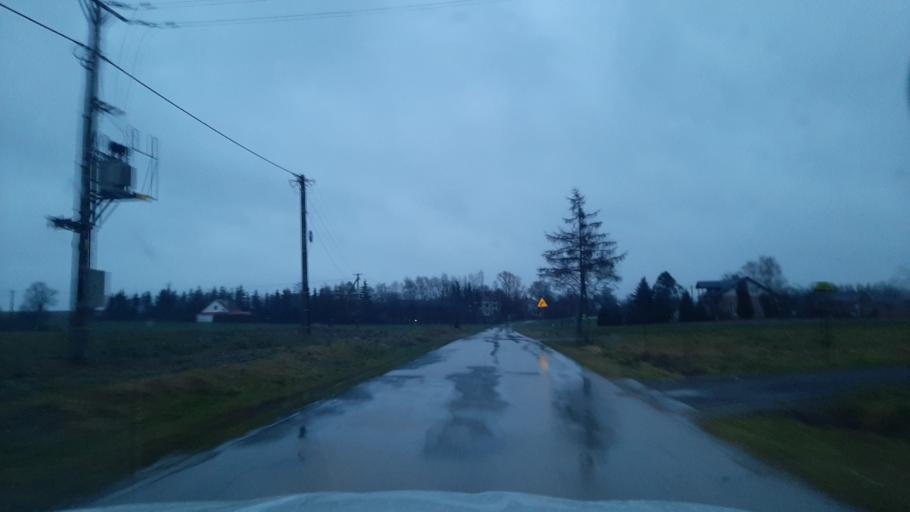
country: PL
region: Lublin Voivodeship
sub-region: Powiat lubelski
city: Jastkow
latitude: 51.3614
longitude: 22.4366
